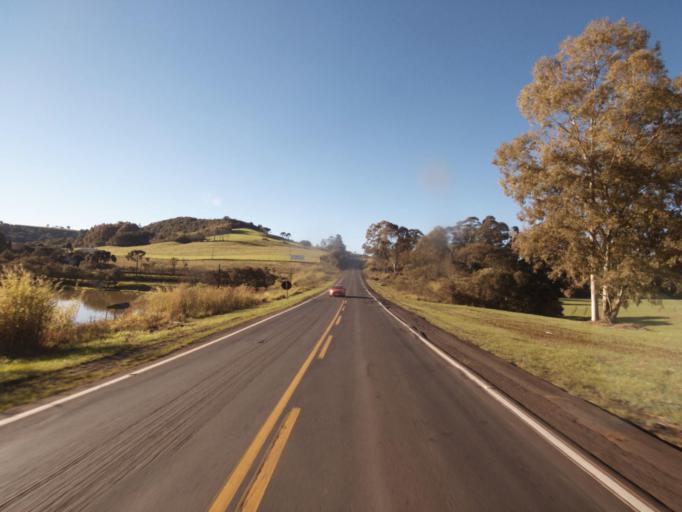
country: AR
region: Misiones
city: Bernardo de Irigoyen
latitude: -26.3359
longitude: -53.5460
